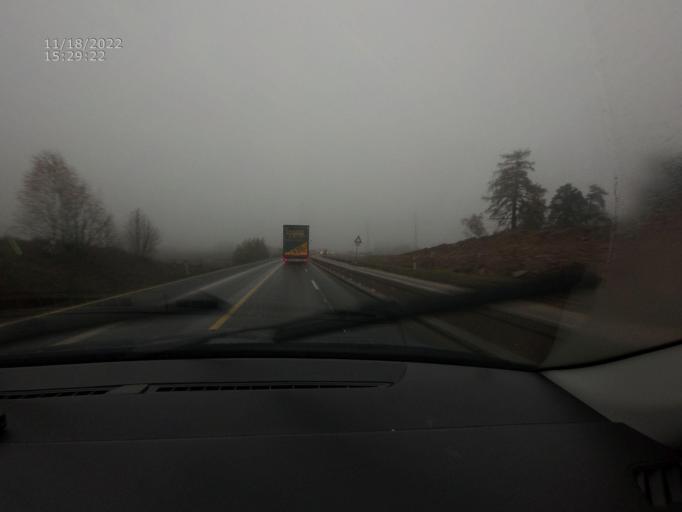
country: CZ
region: Central Bohemia
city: Milin
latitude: 49.6468
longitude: 14.0510
